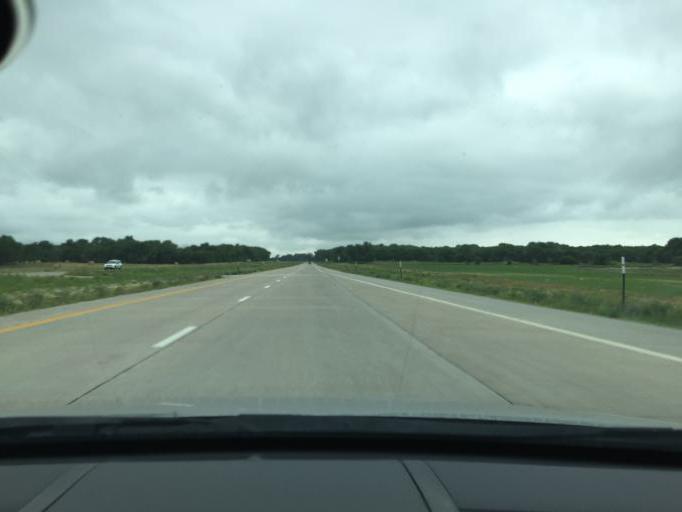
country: US
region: Kansas
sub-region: Reno County
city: Buhler
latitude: 38.1515
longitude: -97.8539
